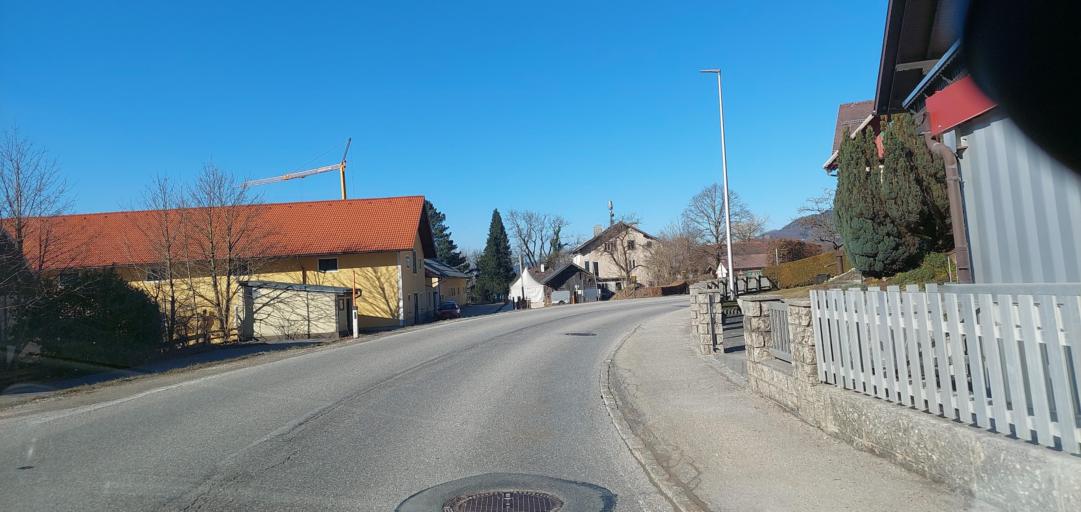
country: AT
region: Upper Austria
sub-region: Politischer Bezirk Vocklabruck
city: Steinbach am Attersee
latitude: 47.7989
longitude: 13.5396
